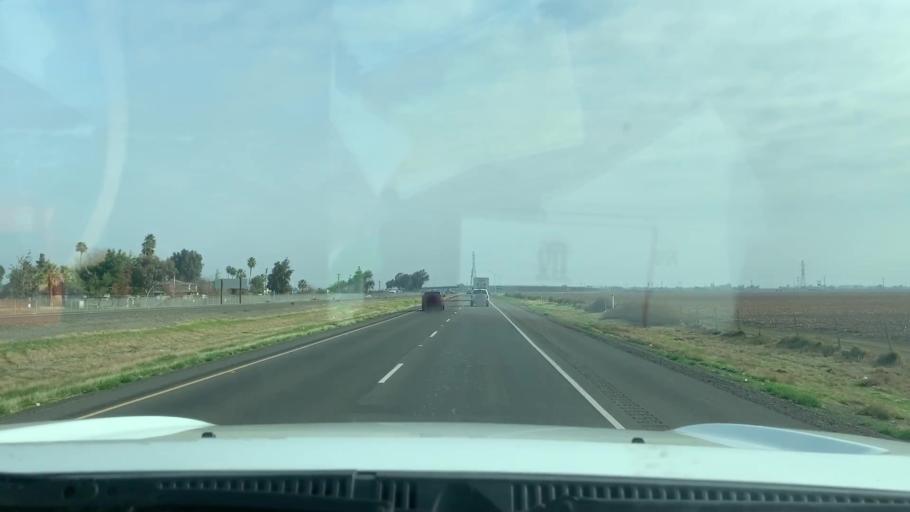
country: US
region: California
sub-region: Kings County
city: Lemoore Station
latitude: 36.2554
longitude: -119.8793
